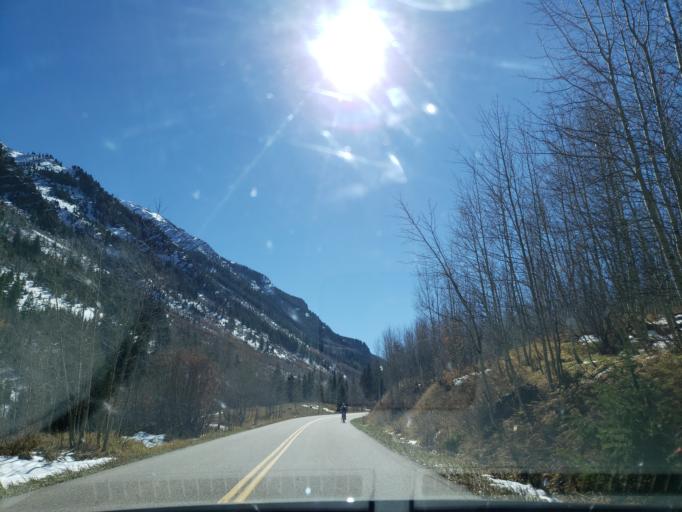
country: US
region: Colorado
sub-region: Pitkin County
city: Snowmass Village
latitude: 39.1453
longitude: -106.8940
